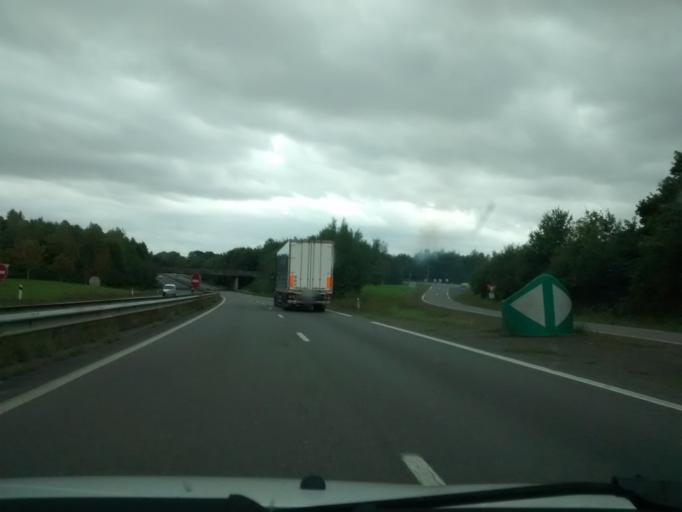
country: FR
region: Brittany
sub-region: Departement d'Ille-et-Vilaine
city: La Meziere
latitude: 48.2061
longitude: -1.7357
